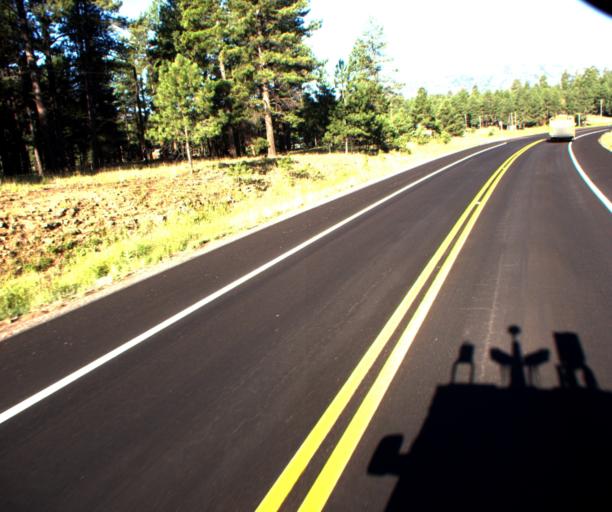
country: US
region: Arizona
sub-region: Apache County
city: Eagar
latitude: 33.8275
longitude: -109.1106
